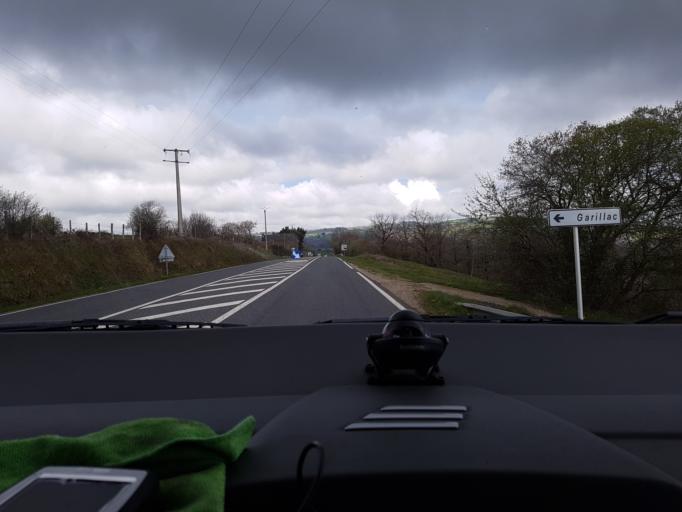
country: FR
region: Midi-Pyrenees
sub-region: Departement de l'Aveyron
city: Moyrazes
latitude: 44.3835
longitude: 2.4054
